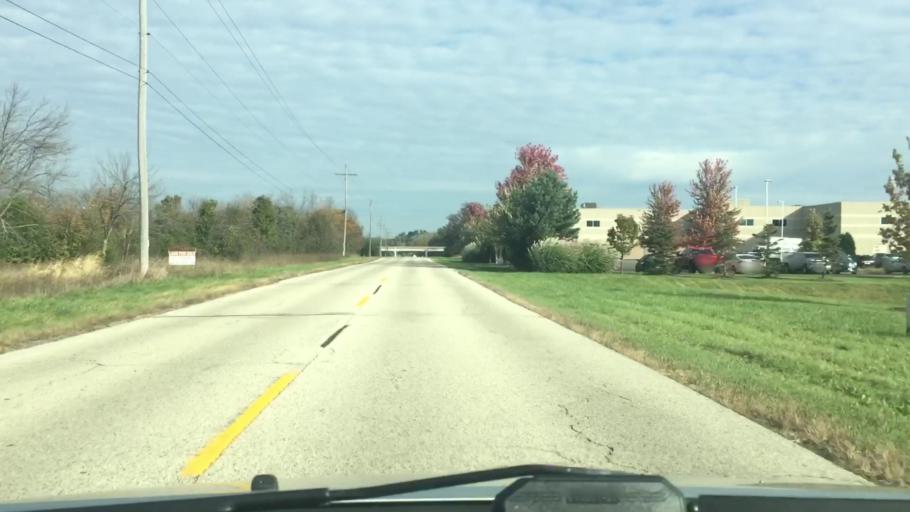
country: US
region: Wisconsin
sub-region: Waukesha County
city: Oconomowoc
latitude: 43.0652
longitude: -88.4813
